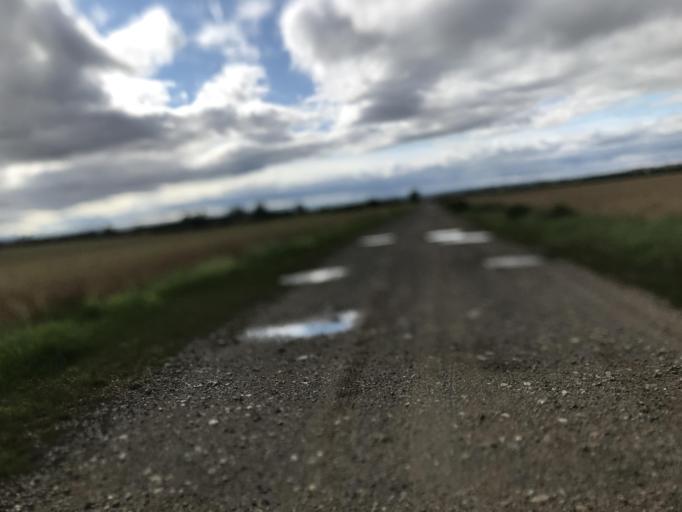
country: DE
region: Saxony-Anhalt
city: Ditfurt
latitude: 51.8131
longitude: 11.2336
